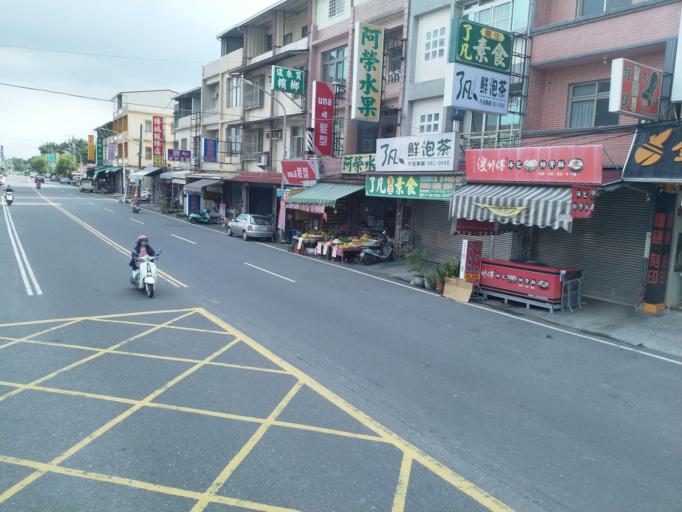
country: TW
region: Taiwan
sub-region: Pingtung
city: Pingtung
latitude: 22.8986
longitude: 120.5422
